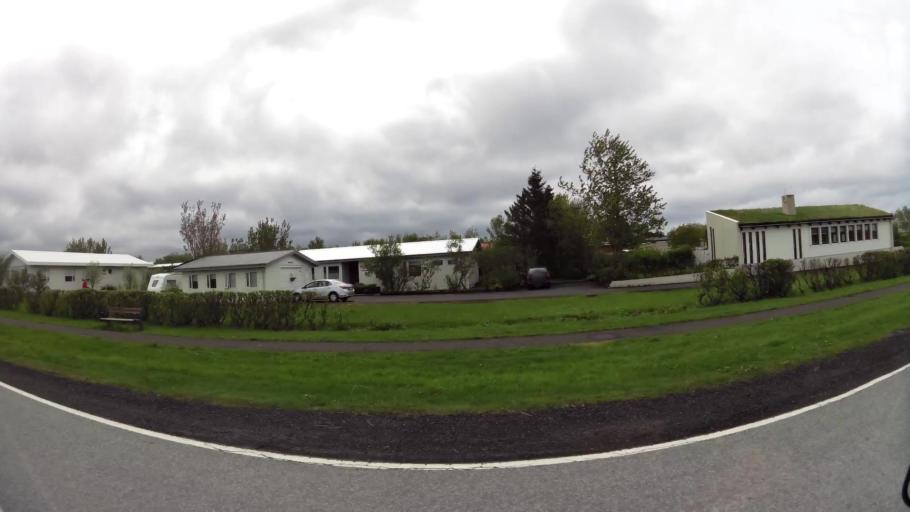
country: IS
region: Capital Region
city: Alftanes
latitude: 64.1094
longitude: -22.0136
